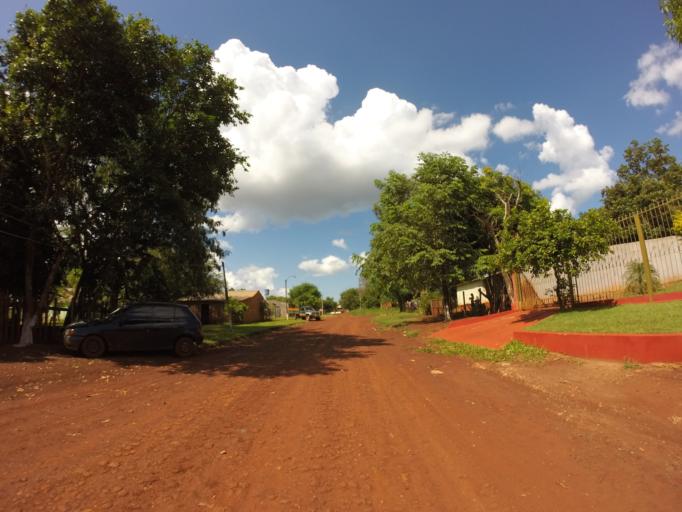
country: PY
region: Alto Parana
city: Ciudad del Este
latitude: -25.3716
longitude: -54.6499
